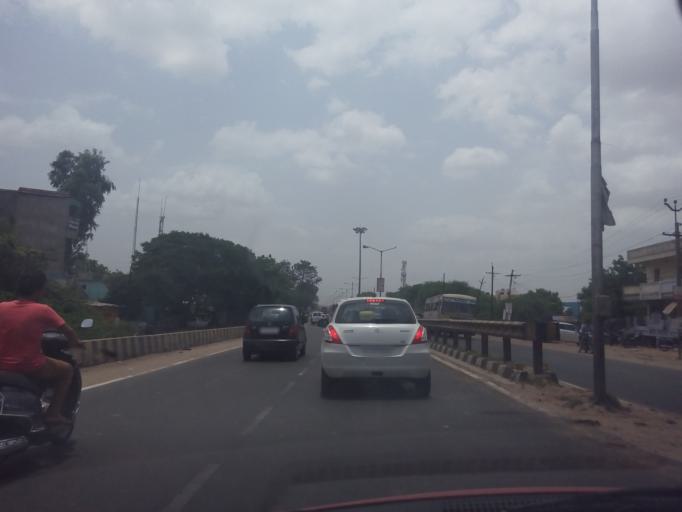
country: IN
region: Gujarat
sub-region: Ahmadabad
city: Sanand
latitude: 22.9880
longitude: 72.3849
